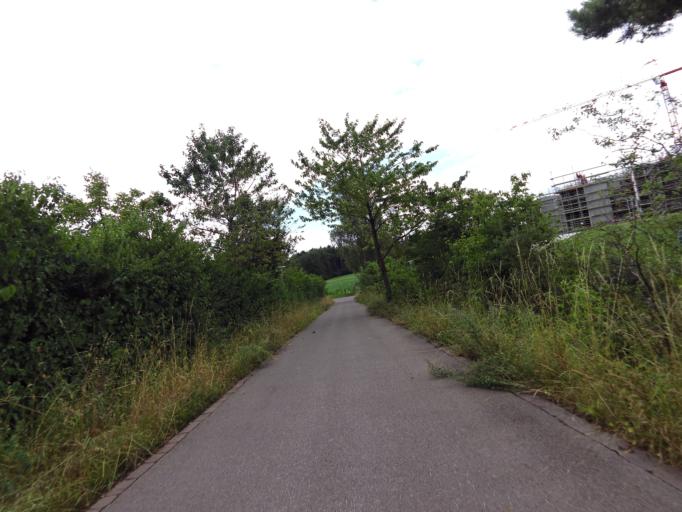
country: CH
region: Zurich
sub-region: Bezirk Zuerich
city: Zuerich (Kreis 10)
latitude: 47.4065
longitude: 8.5034
